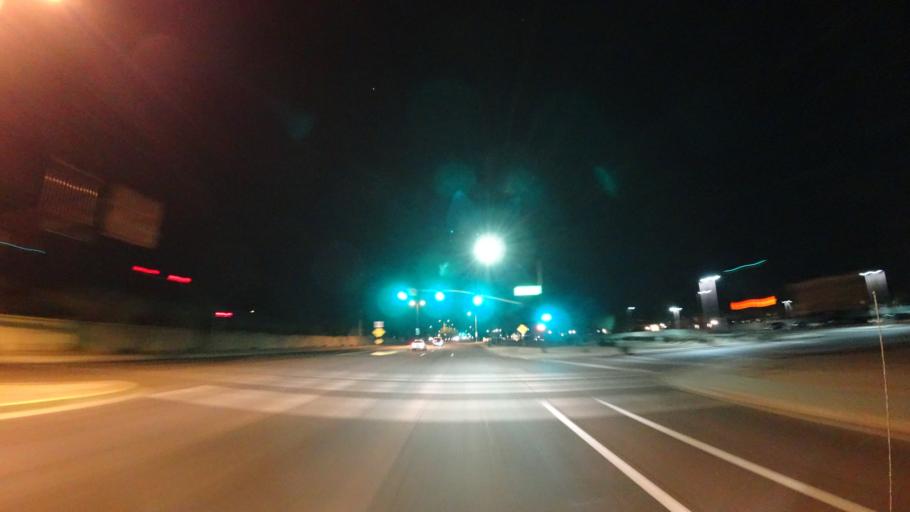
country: US
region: Arizona
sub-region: Maricopa County
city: San Carlos
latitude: 33.3395
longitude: -111.8244
